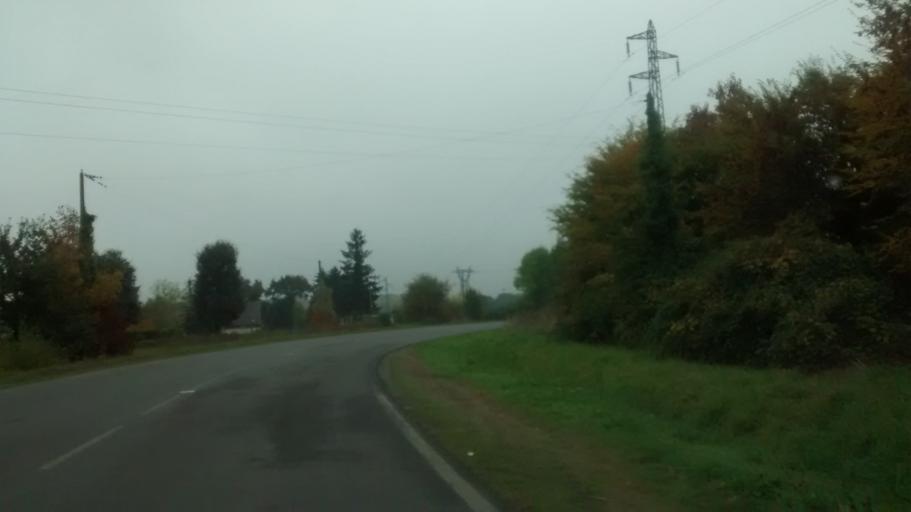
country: FR
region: Brittany
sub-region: Departement d'Ille-et-Vilaine
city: Pace
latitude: 48.1488
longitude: -1.7956
